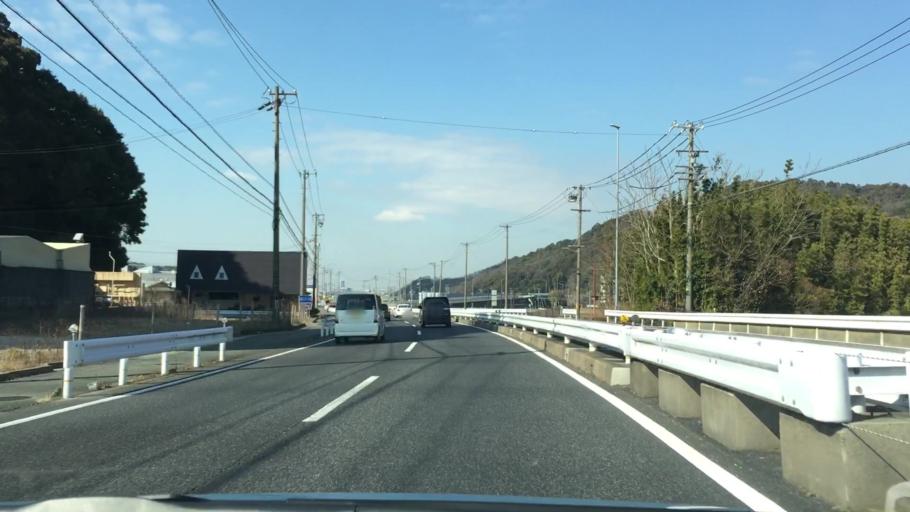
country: JP
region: Aichi
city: Gamagori
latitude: 34.9056
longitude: 137.2335
